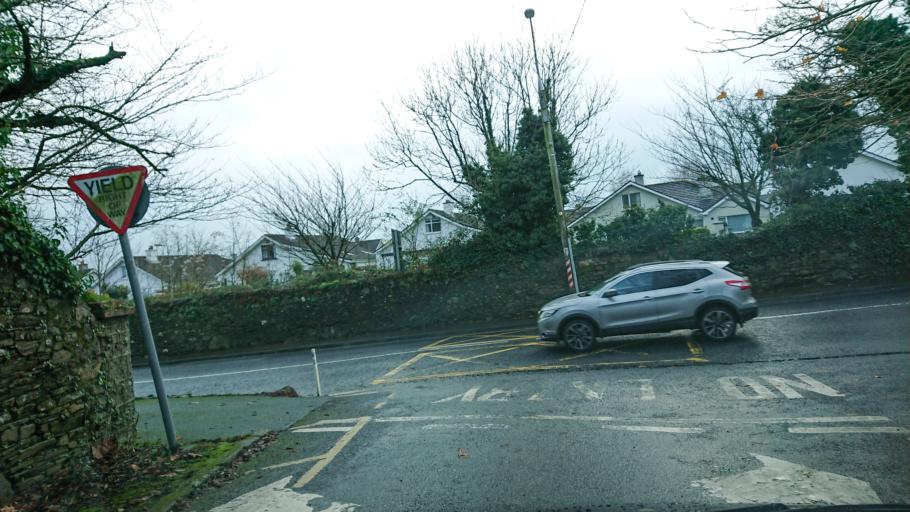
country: IE
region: Munster
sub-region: Waterford
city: Waterford
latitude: 52.2469
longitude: -7.0768
